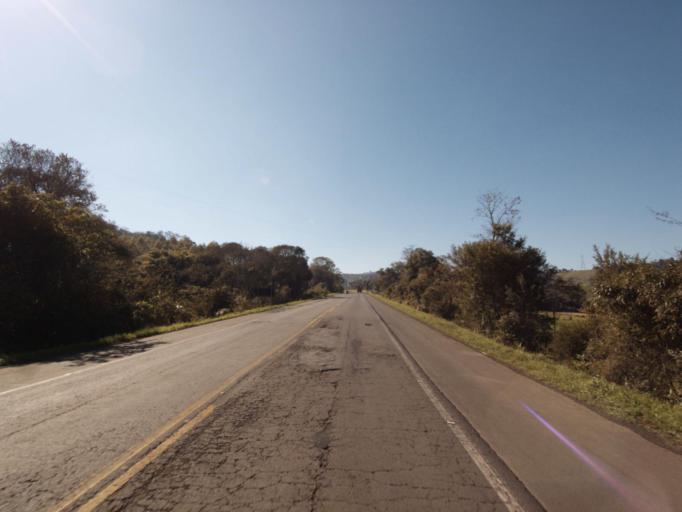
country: BR
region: Rio Grande do Sul
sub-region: Frederico Westphalen
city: Frederico Westphalen
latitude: -27.0669
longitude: -53.2267
